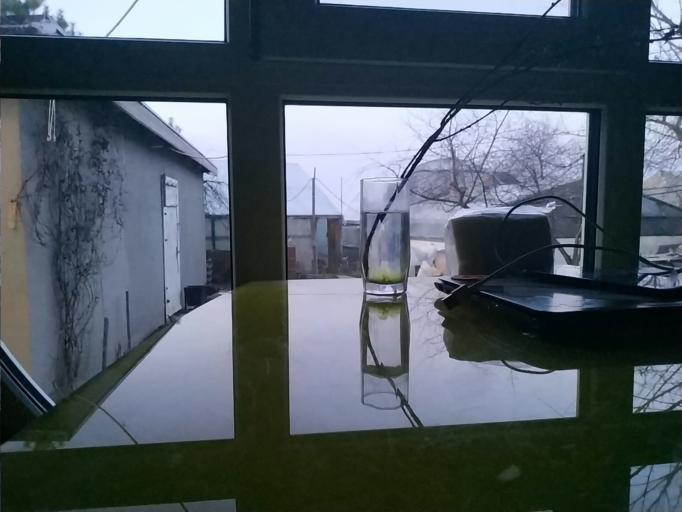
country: RU
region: Republic of Karelia
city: Sukkozero
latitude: 62.7378
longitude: 31.8725
